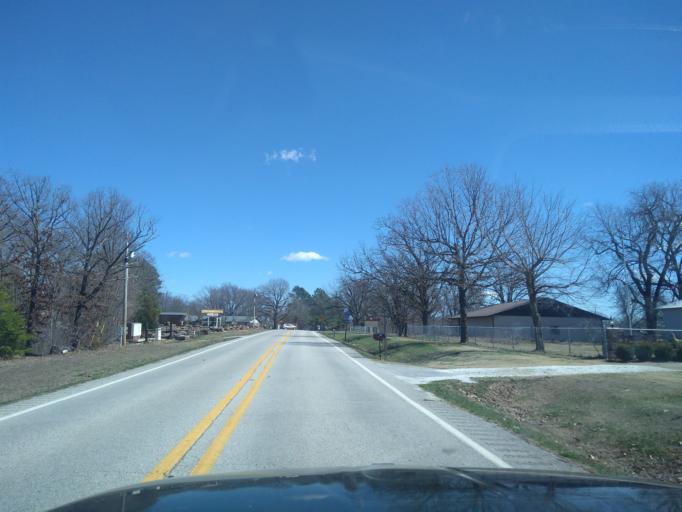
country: US
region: Arkansas
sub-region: Washington County
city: Farmington
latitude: 36.0808
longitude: -94.3026
